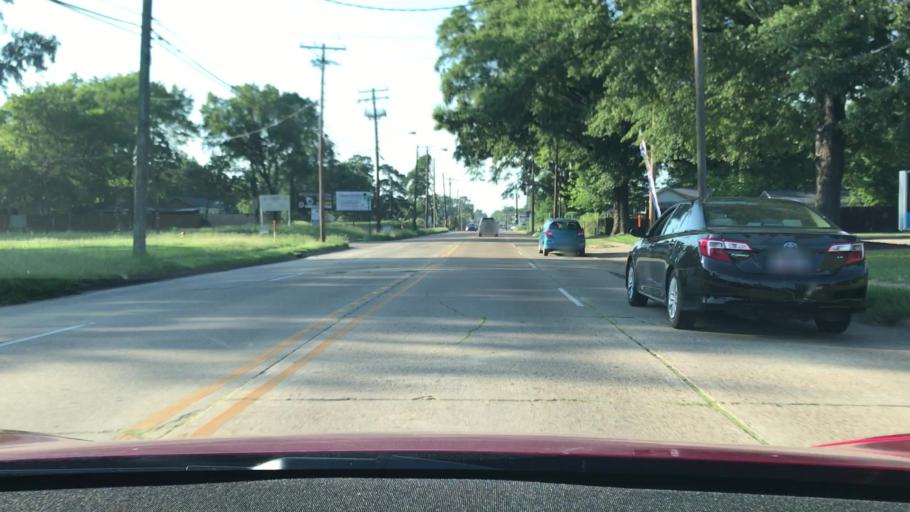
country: US
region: Louisiana
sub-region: Bossier Parish
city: Bossier City
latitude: 32.4436
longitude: -93.7460
